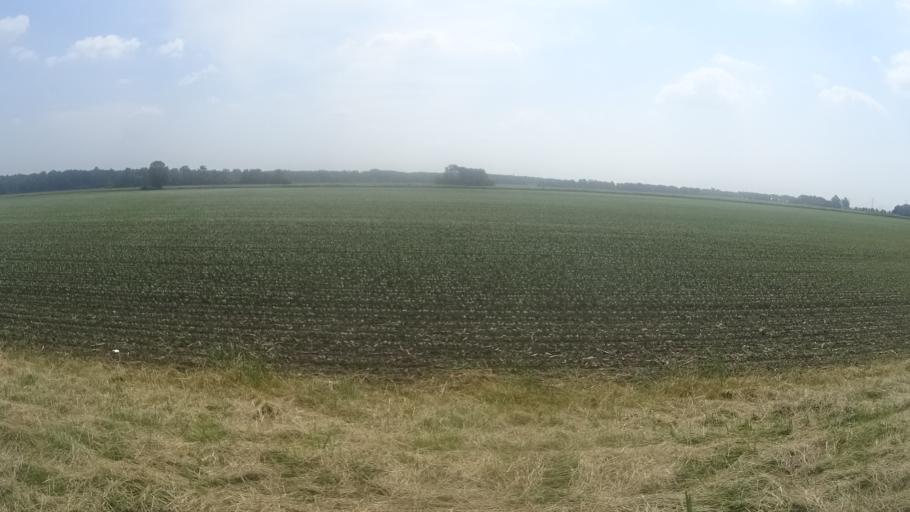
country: US
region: Ohio
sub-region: Erie County
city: Sandusky
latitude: 41.3518
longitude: -82.6942
